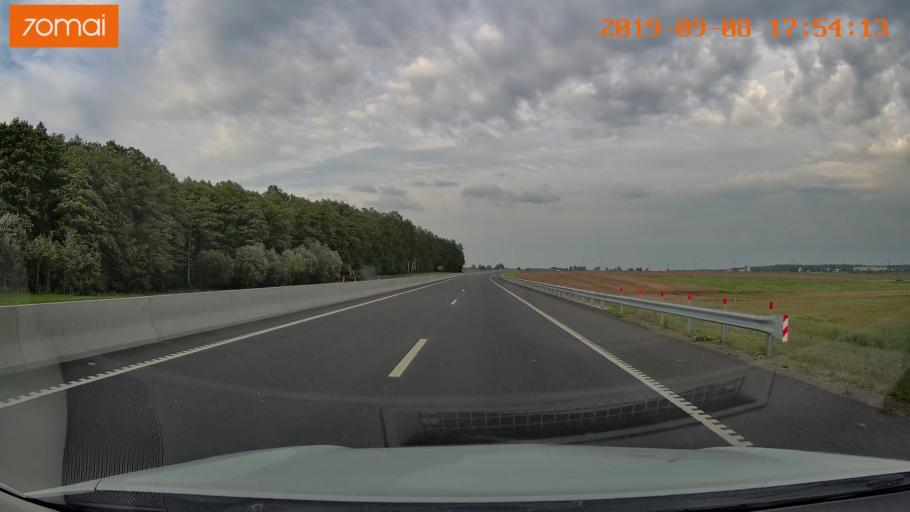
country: BY
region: Grodnenskaya
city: Shchuchin
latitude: 53.7196
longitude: 24.9581
